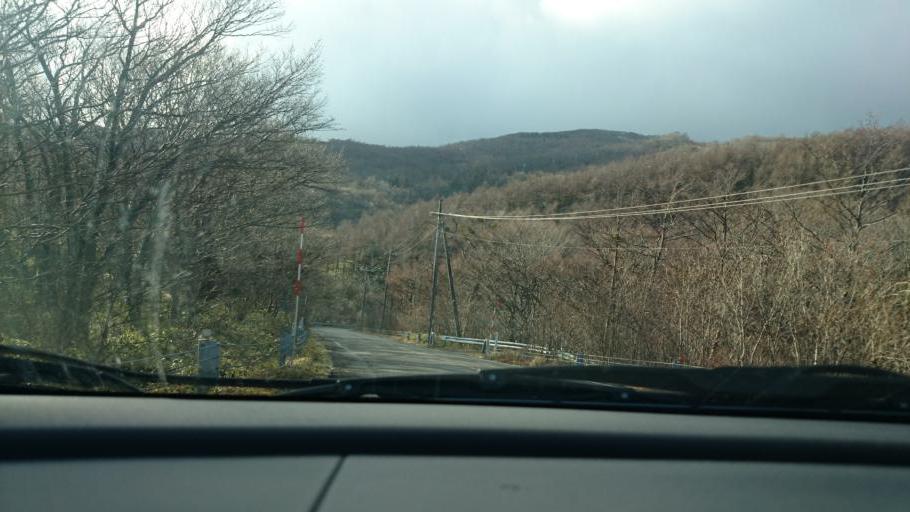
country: JP
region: Tochigi
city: Kuroiso
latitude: 37.1462
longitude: 140.0170
